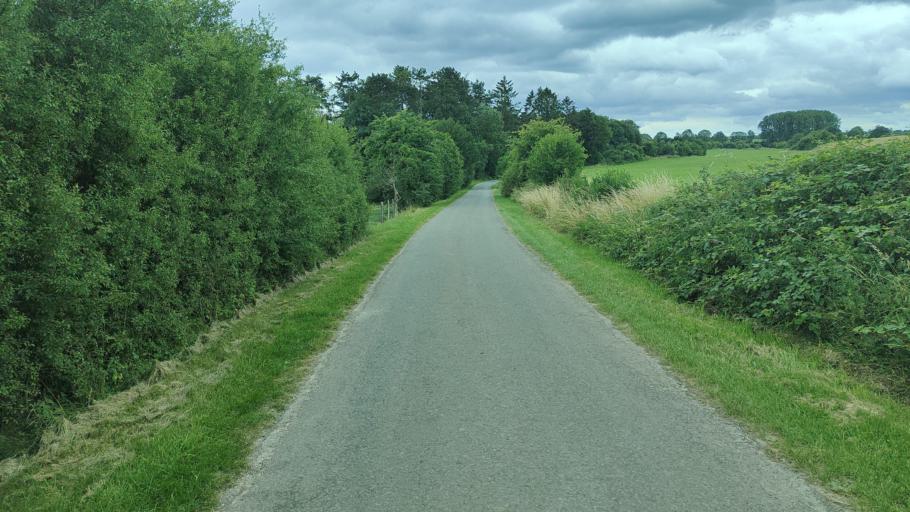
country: BE
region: Wallonia
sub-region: Province du Hainaut
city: Chimay
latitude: 50.0599
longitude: 4.3637
